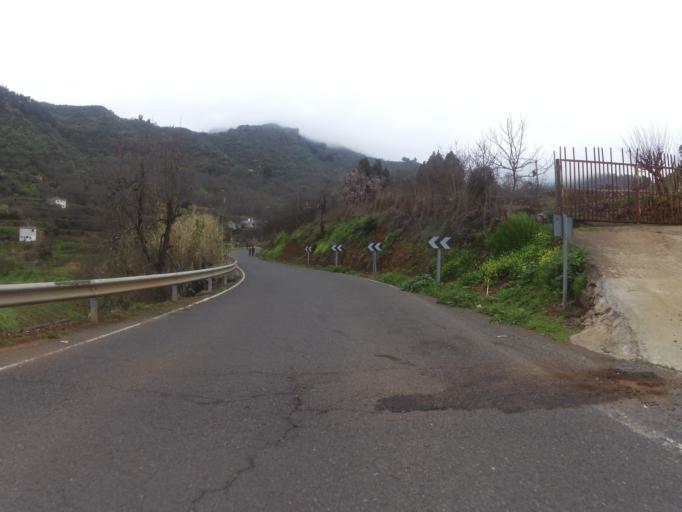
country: ES
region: Canary Islands
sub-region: Provincia de Las Palmas
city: Vega de San Mateo
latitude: 28.0022
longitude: -15.5410
